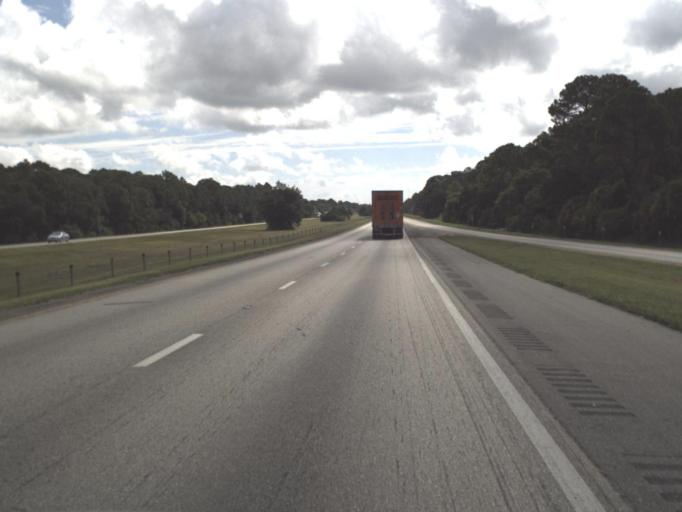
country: US
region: Florida
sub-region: Sarasota County
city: North Port
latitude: 27.0991
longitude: -82.2001
